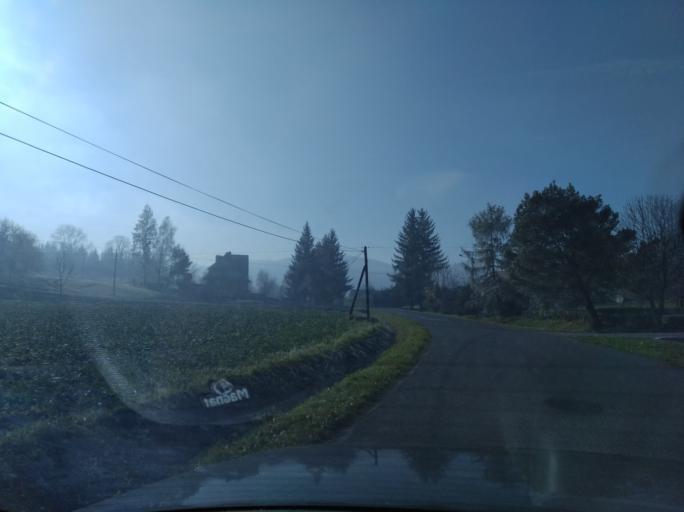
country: PL
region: Subcarpathian Voivodeship
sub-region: Powiat strzyzowski
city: Wysoka Strzyzowska
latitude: 49.8526
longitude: 21.7020
